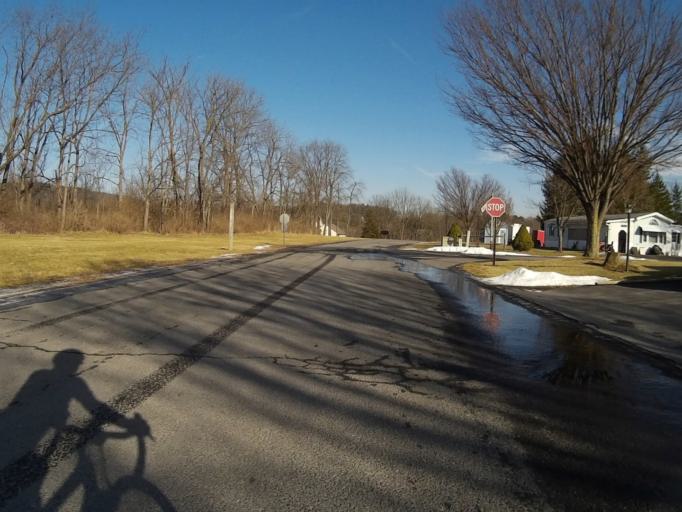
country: US
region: Pennsylvania
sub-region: Centre County
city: Houserville
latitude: 40.8734
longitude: -77.8626
